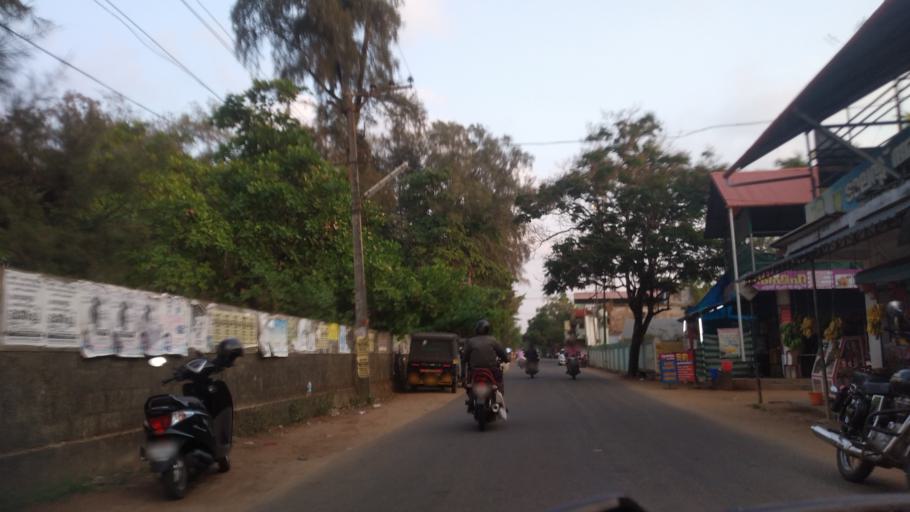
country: IN
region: Kerala
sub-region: Thrissur District
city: Kodungallur
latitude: 10.2681
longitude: 76.1417
